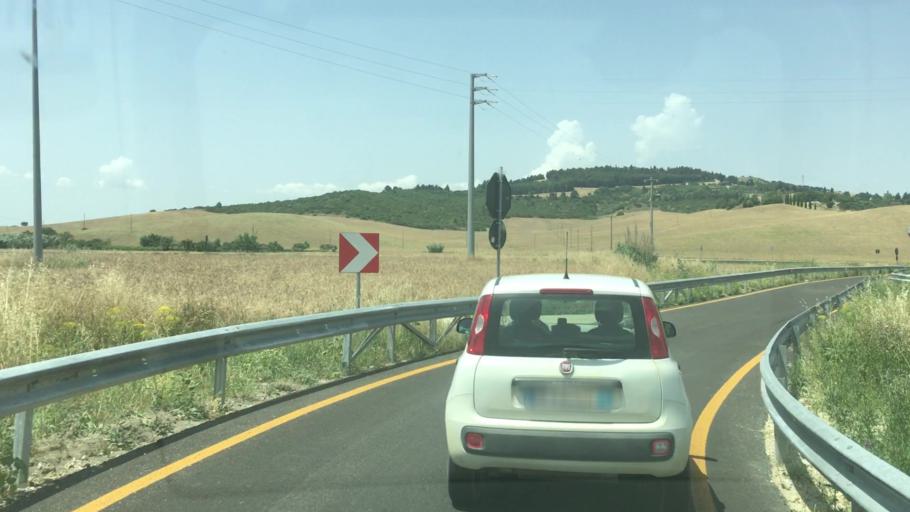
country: IT
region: Basilicate
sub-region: Provincia di Matera
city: La Martella
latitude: 40.6719
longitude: 16.4928
